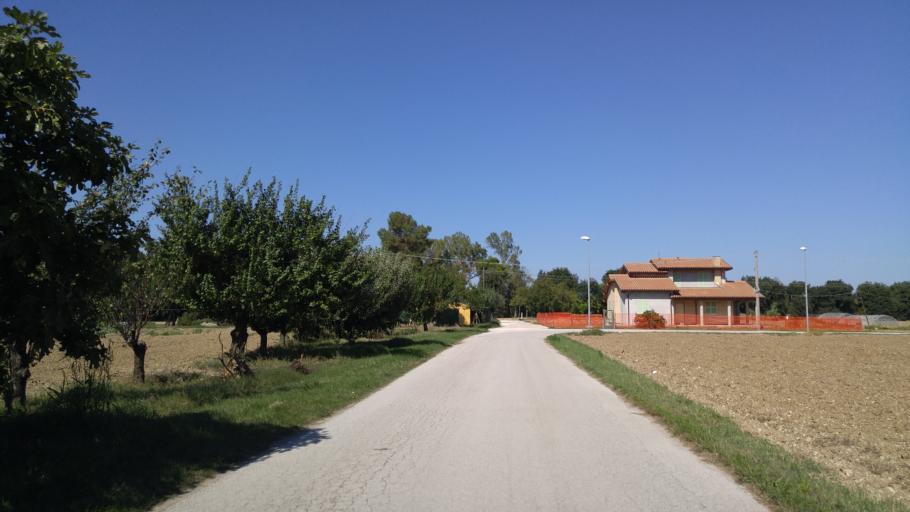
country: IT
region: The Marches
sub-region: Provincia di Pesaro e Urbino
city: Villanova
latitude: 43.7516
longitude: 12.9374
